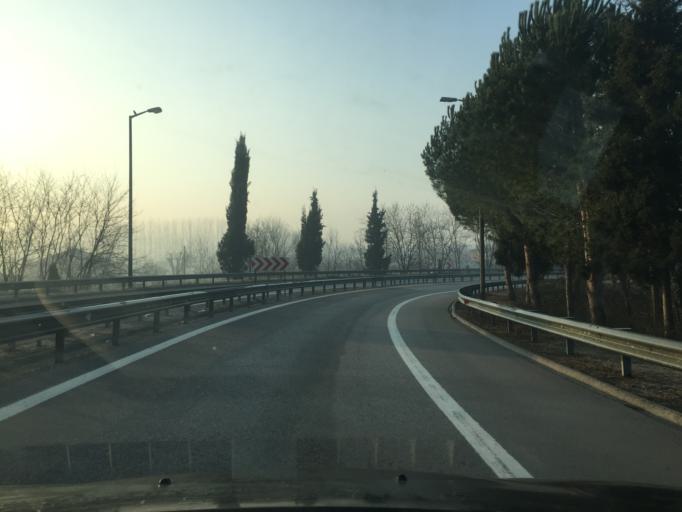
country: TR
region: Sakarya
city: Akyazi
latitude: 40.7163
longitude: 30.5683
